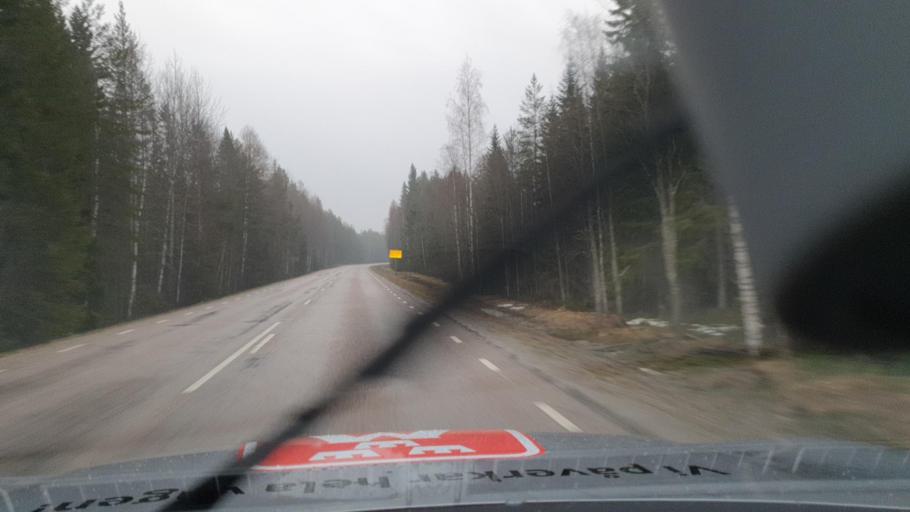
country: SE
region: Vaesternorrland
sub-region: OErnskoeldsviks Kommun
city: Bjasta
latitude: 63.2262
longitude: 18.4574
